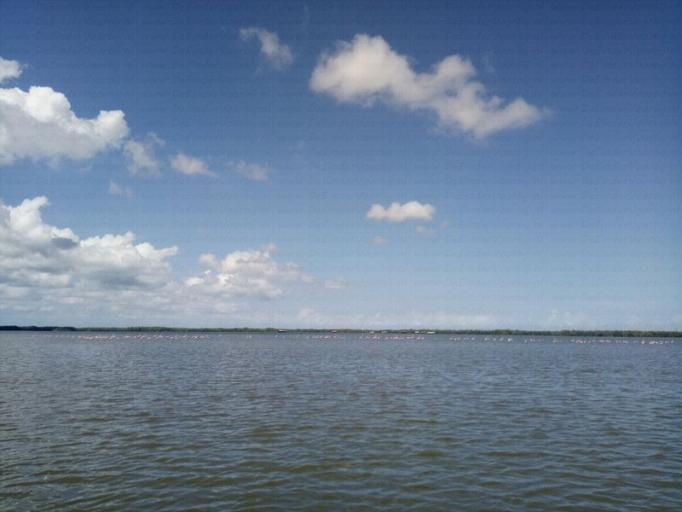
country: SR
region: Nickerie
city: Nieuw Nickerie
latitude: 5.9578
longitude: -56.8494
